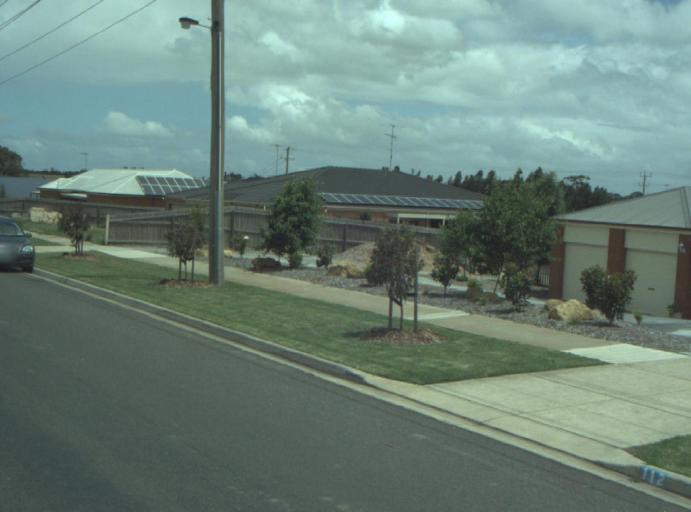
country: AU
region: Victoria
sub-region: Greater Geelong
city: Wandana Heights
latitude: -38.2137
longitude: 144.3015
